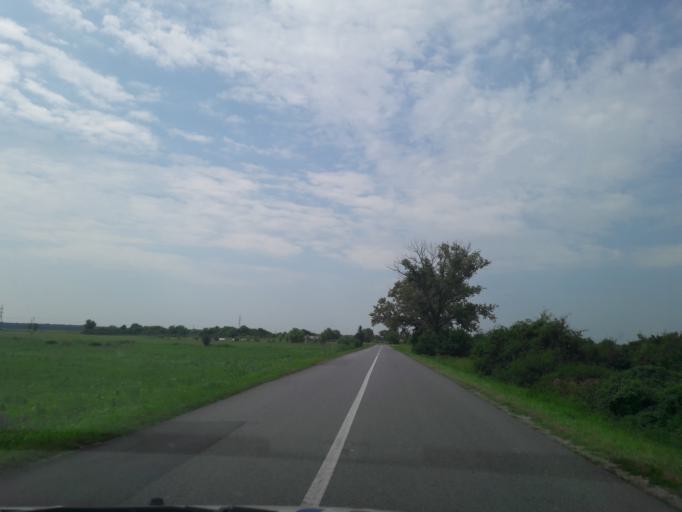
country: HR
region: Osjecko-Baranjska
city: Bizovac
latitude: 45.5055
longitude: 18.4520
